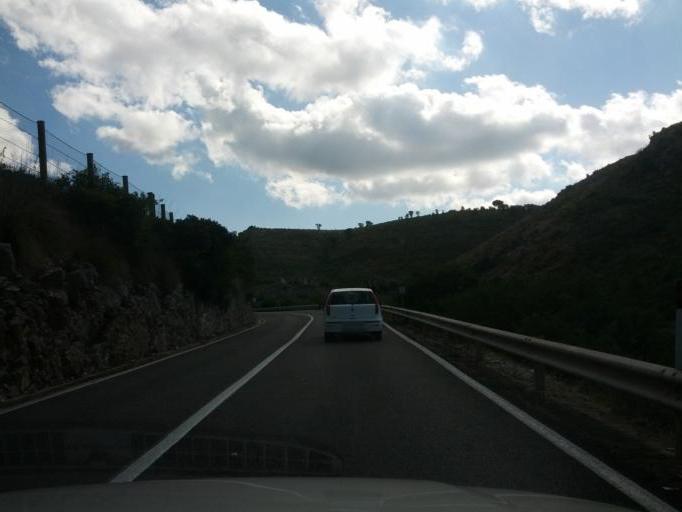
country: IT
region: Latium
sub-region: Provincia di Latina
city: Itri
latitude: 41.3159
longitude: 13.4852
